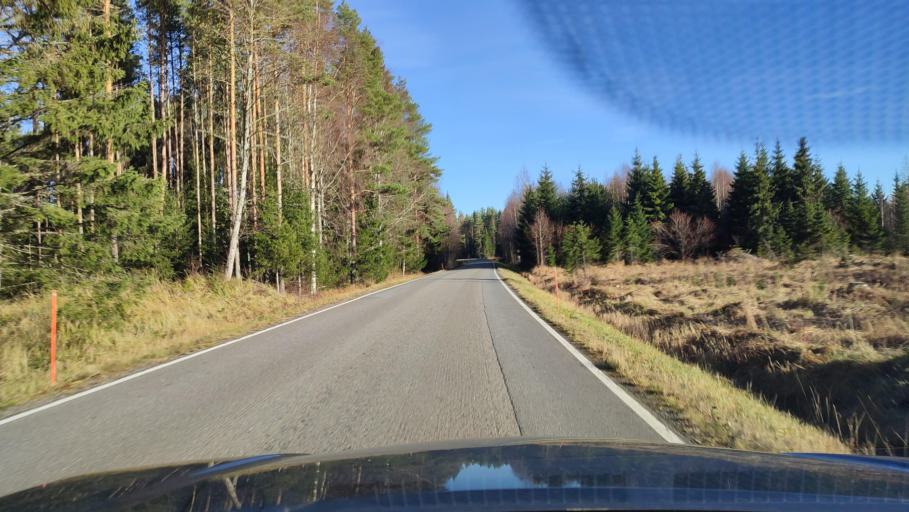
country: FI
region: Southern Ostrobothnia
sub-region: Suupohja
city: Teuva
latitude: 62.4151
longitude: 21.7047
